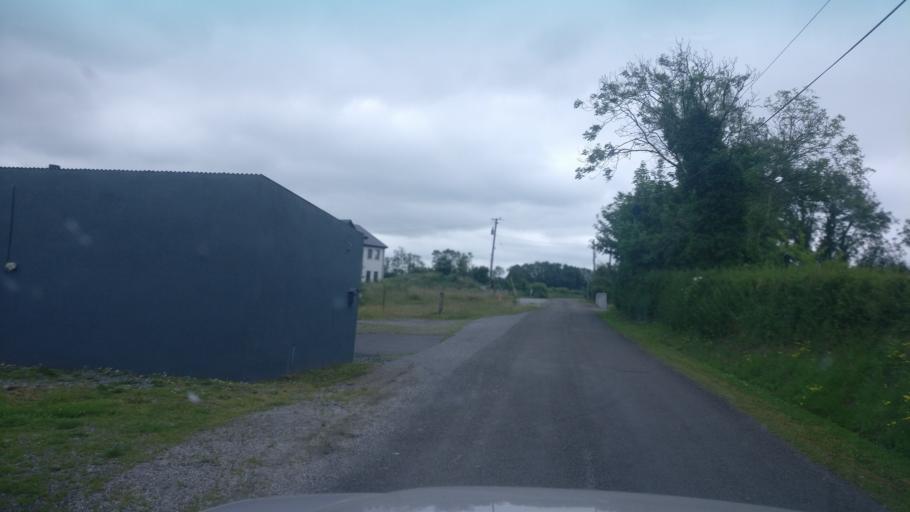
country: IE
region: Connaught
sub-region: County Galway
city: Ballinasloe
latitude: 53.2961
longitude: -8.3415
